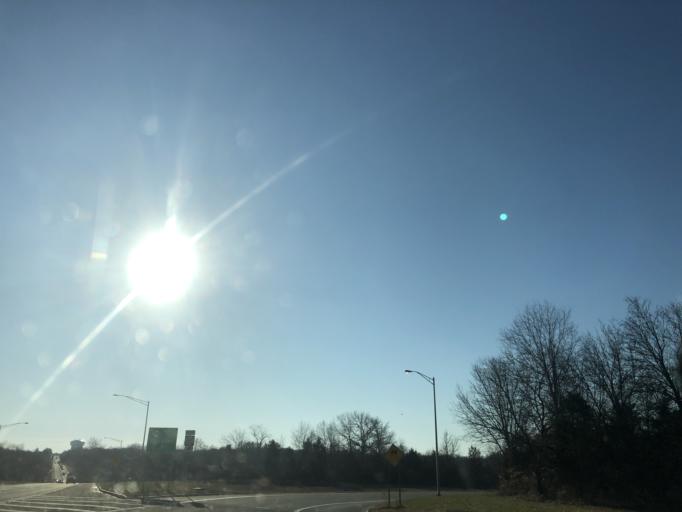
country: US
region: New Jersey
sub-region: Gloucester County
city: Wenonah
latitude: 39.7938
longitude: -75.1138
